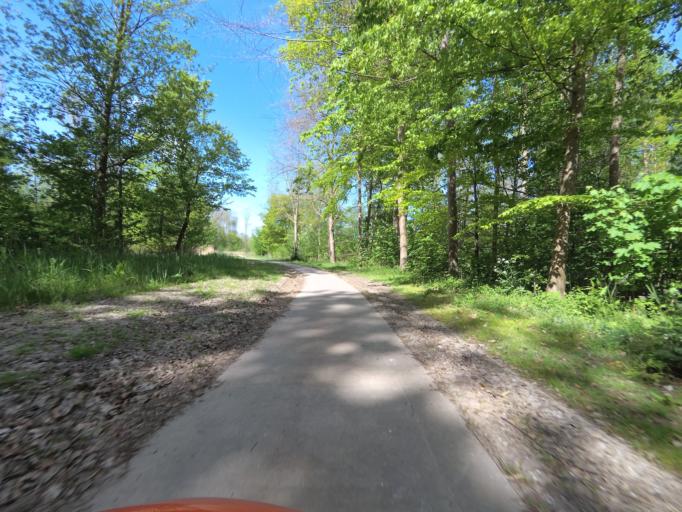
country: NL
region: Flevoland
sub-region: Gemeente Dronten
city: Dronten
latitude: 52.5184
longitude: 5.6404
